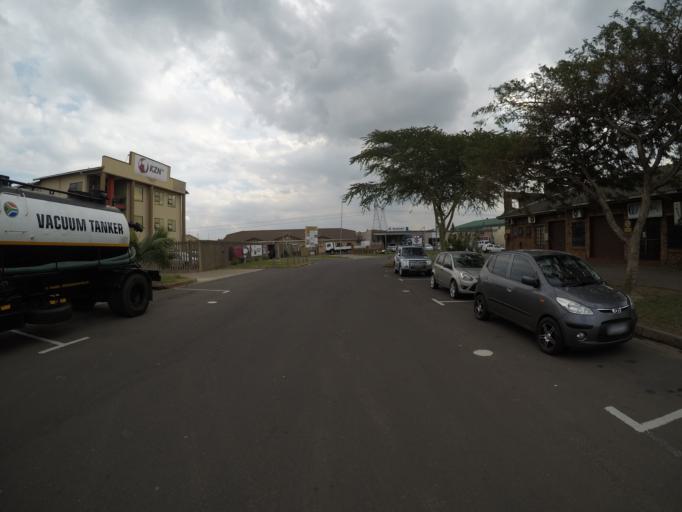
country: ZA
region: KwaZulu-Natal
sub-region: uThungulu District Municipality
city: Richards Bay
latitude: -28.7603
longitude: 32.0418
